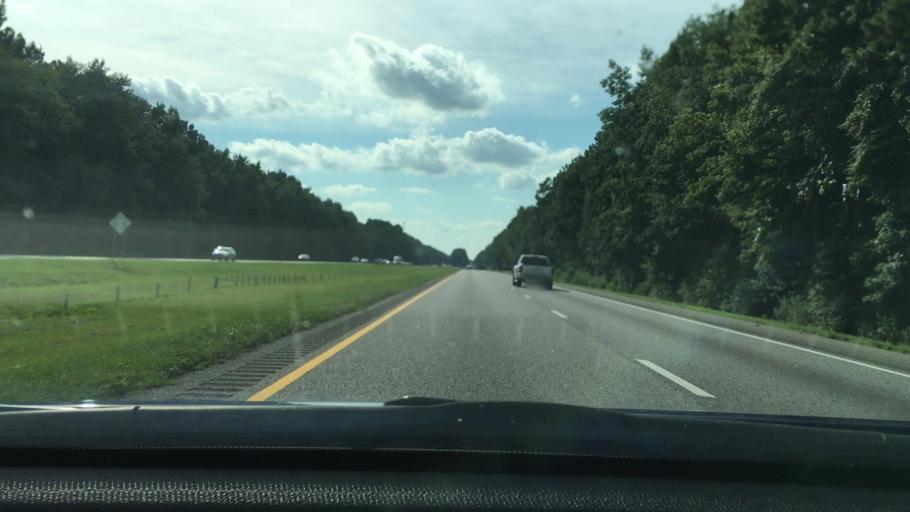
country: US
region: South Carolina
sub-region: Dorchester County
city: Ridgeville
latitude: 33.1339
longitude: -80.3033
